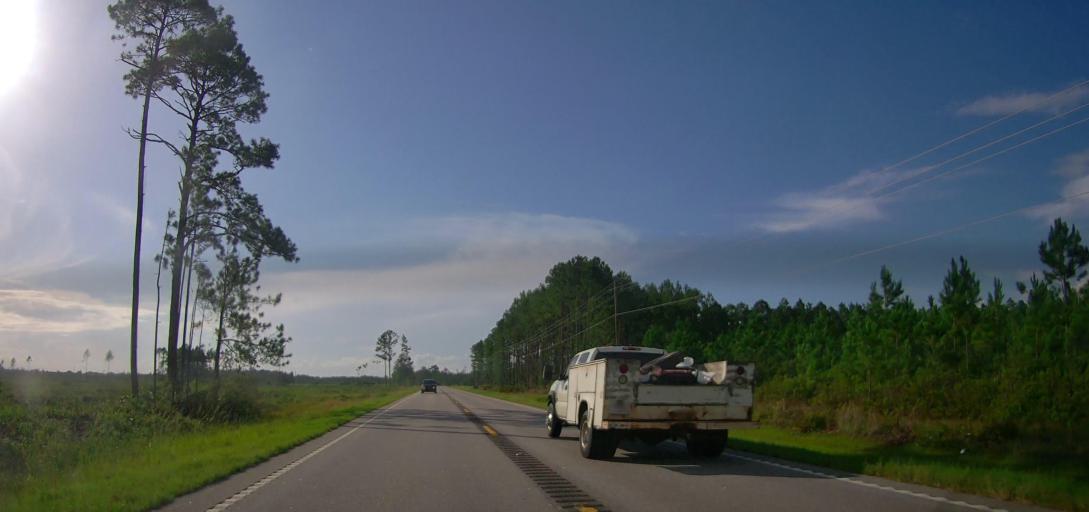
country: US
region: Georgia
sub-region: Coffee County
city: Nicholls
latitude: 31.3769
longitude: -82.6397
